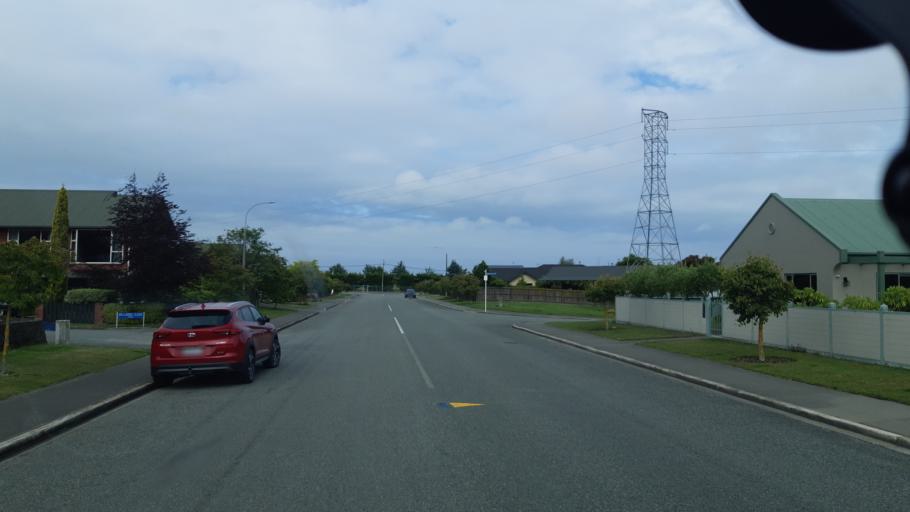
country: NZ
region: Canterbury
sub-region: Timaru District
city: Timaru
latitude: -44.3818
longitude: 171.2019
